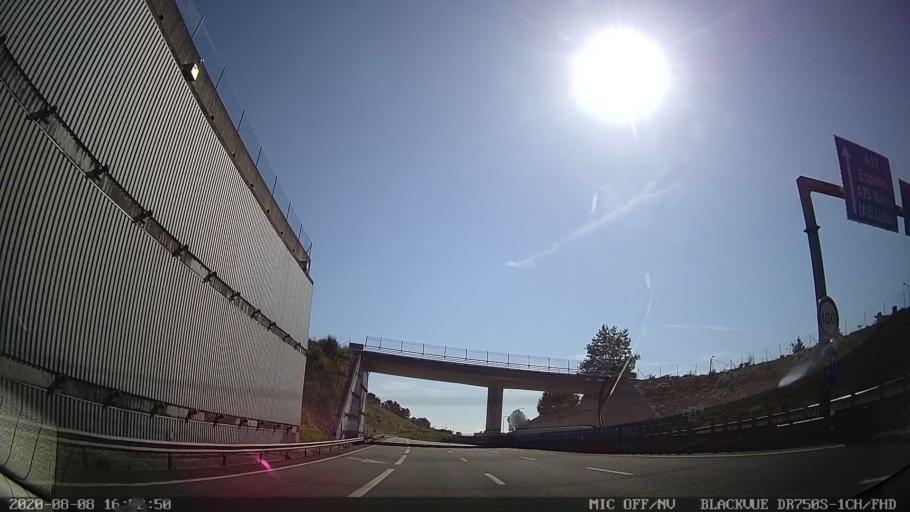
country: PT
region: Porto
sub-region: Vila Nova de Gaia
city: Canelas
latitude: 41.0915
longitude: -8.5930
